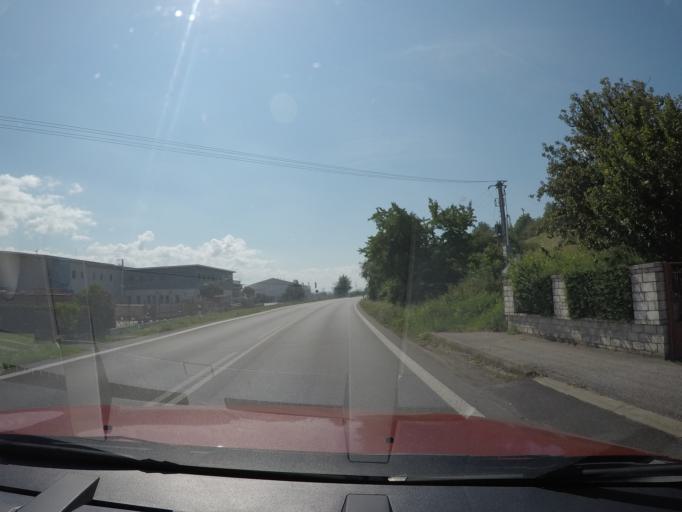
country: SK
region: Presovsky
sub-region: Okres Presov
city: Presov
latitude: 48.8716
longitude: 21.2504
